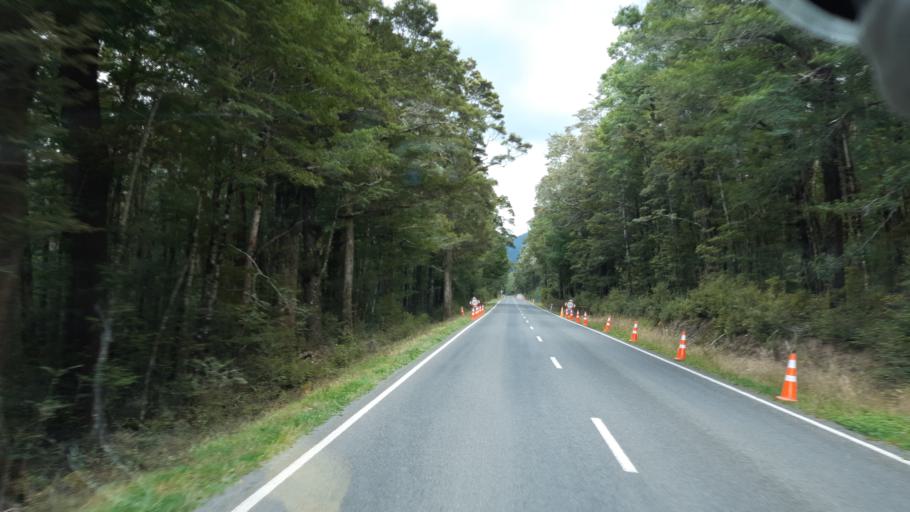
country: NZ
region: Canterbury
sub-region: Hurunui District
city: Amberley
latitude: -42.4889
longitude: 172.3879
